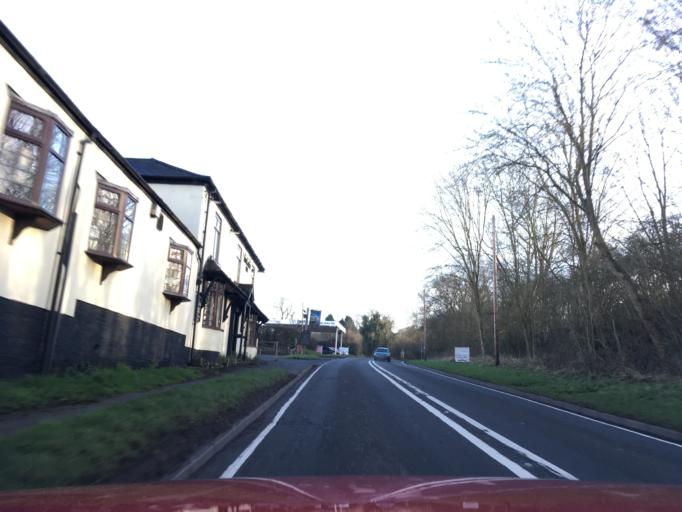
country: GB
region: England
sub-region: Warwickshire
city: Henley in Arden
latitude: 52.2646
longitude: -1.7688
